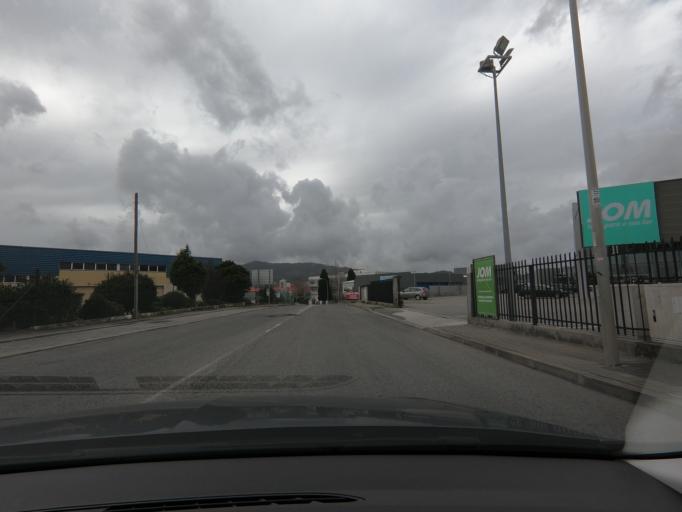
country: PT
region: Lisbon
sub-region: Sintra
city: Rio de Mouro
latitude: 38.7713
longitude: -9.3479
